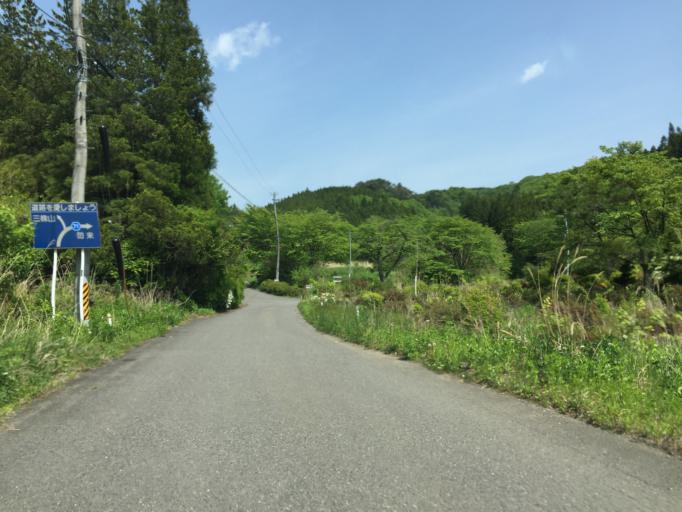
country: JP
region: Fukushima
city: Ishikawa
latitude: 37.0080
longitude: 140.5900
